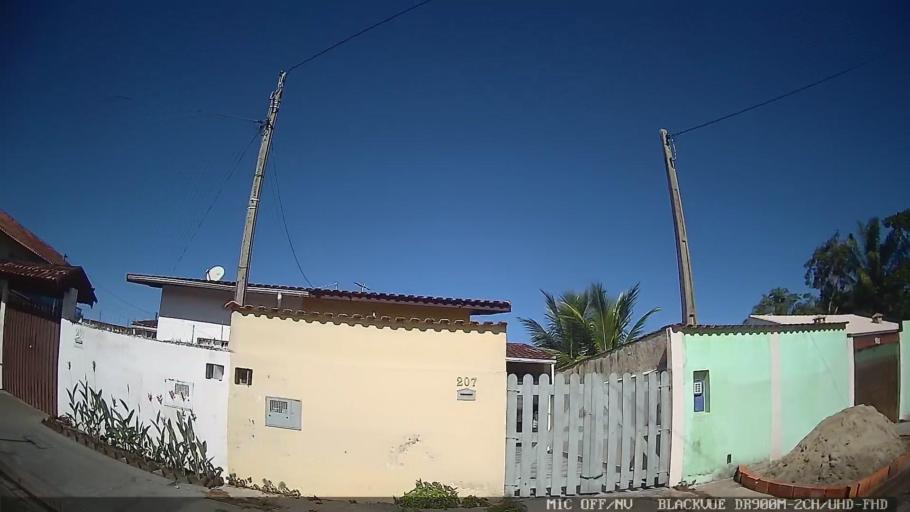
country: BR
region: Sao Paulo
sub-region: Itanhaem
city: Itanhaem
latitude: -24.2207
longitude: -46.8658
